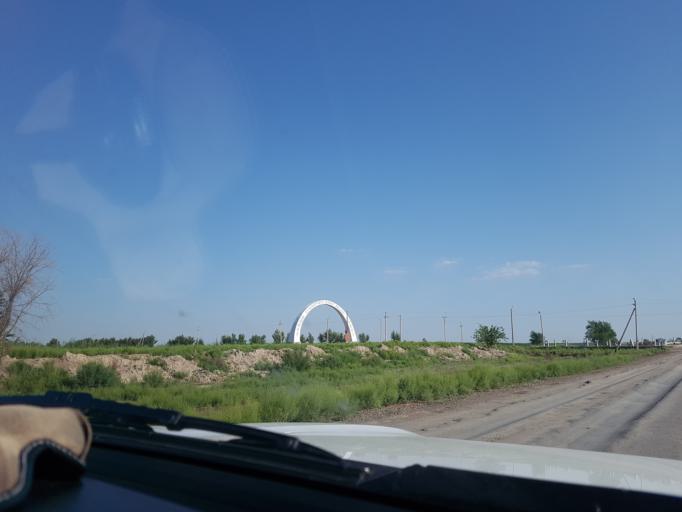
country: TM
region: Dasoguz
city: Koeneuergench
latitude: 41.8616
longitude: 58.7054
